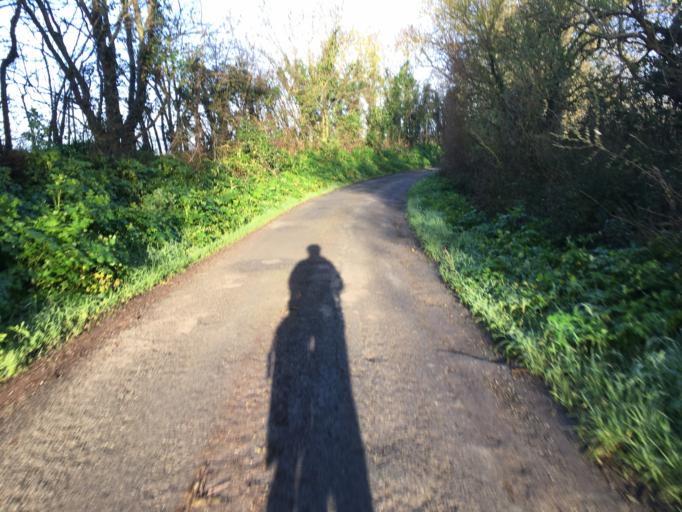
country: FR
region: Poitou-Charentes
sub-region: Departement de la Charente-Maritime
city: Nieul-sur-Mer
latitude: 46.1961
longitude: -1.1752
